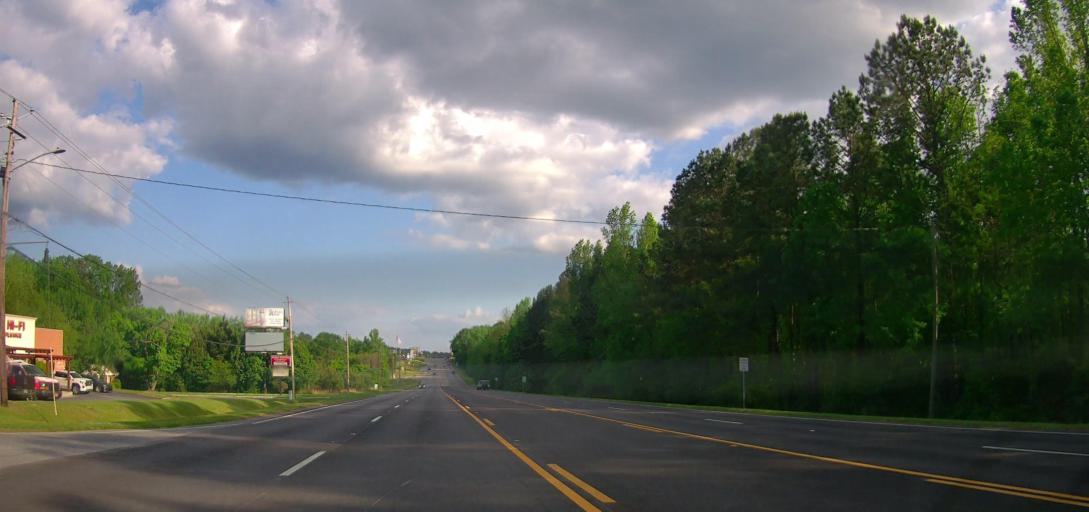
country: US
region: Georgia
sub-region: Baldwin County
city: Milledgeville
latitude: 33.1314
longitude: -83.2688
